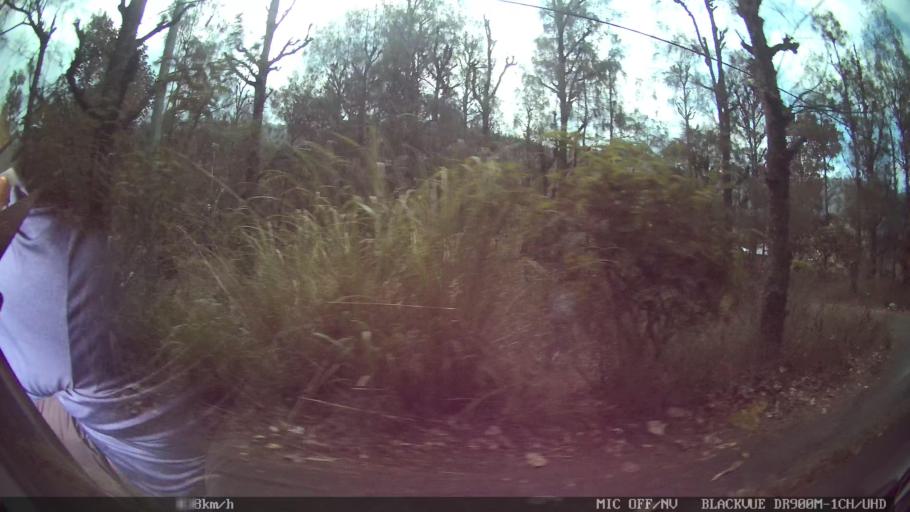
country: ID
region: Bali
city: Banjar Kedisan
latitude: -8.2349
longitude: 115.3555
